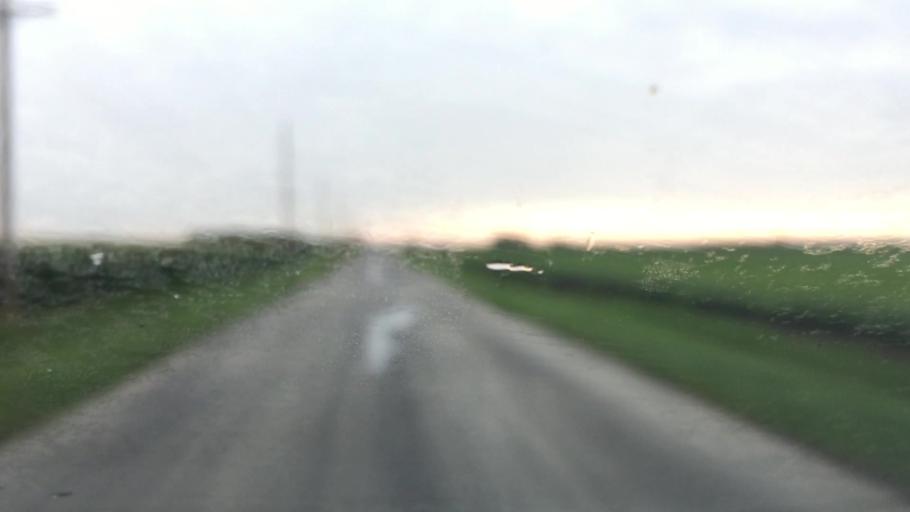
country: US
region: Iowa
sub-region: Lee County
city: Fort Madison
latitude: 40.5569
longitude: -91.2687
